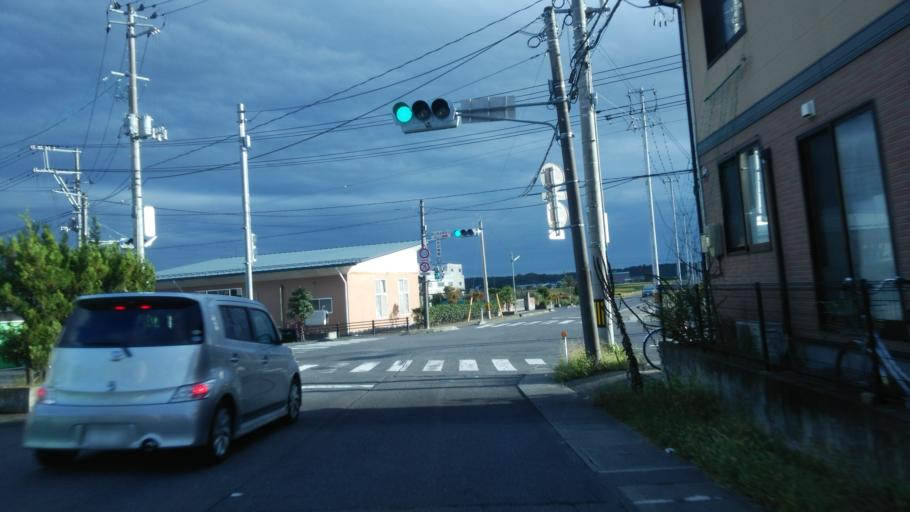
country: JP
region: Fukushima
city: Koriyama
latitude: 37.3742
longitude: 140.3410
